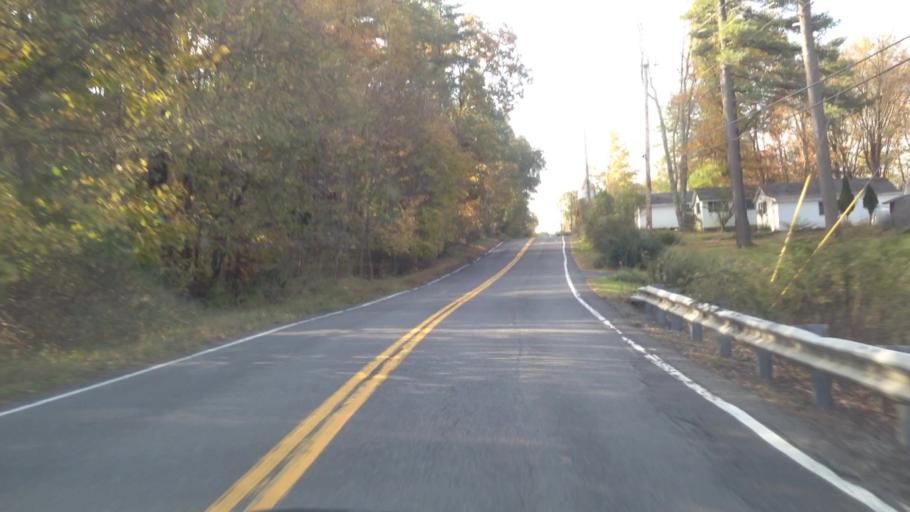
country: US
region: New York
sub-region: Ulster County
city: Tillson
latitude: 41.8338
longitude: -74.0448
